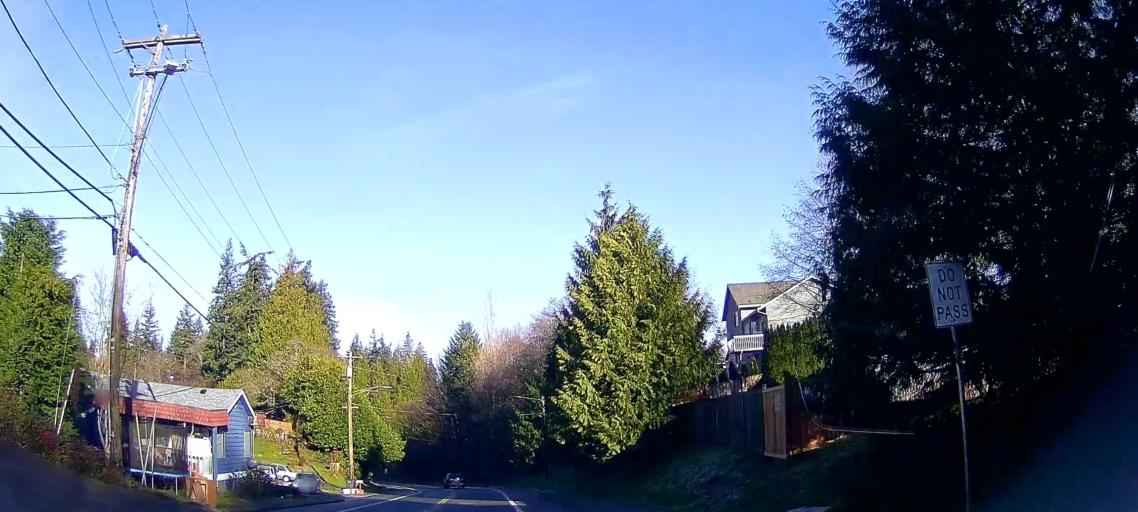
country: US
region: Washington
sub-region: Snohomish County
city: Everett
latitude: 47.9570
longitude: -122.2294
